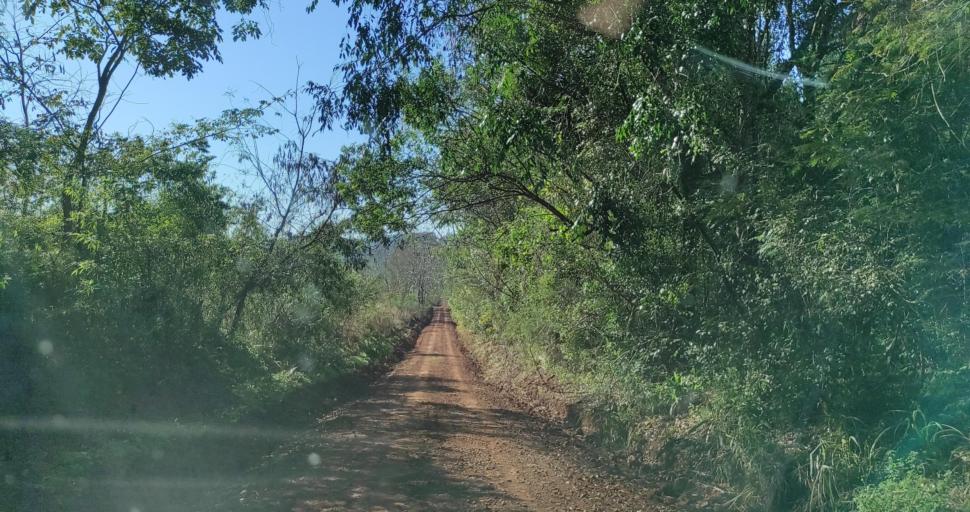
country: AR
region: Misiones
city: Capiovi
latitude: -26.8710
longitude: -55.0382
